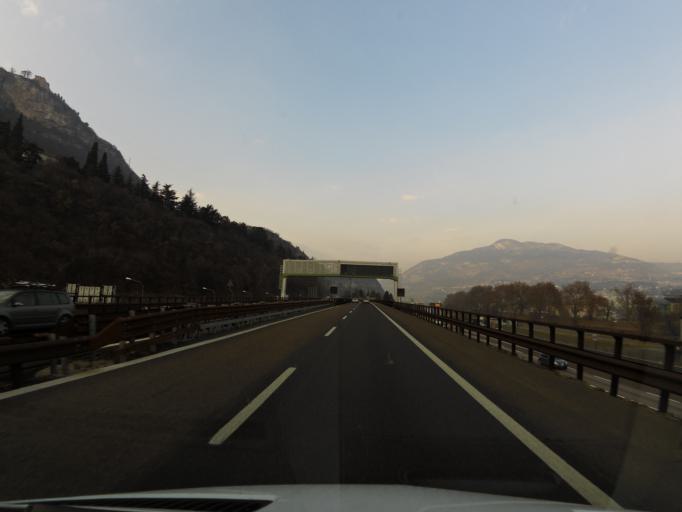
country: IT
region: Trentino-Alto Adige
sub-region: Provincia di Trento
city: Trento
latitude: 46.0599
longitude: 11.1099
